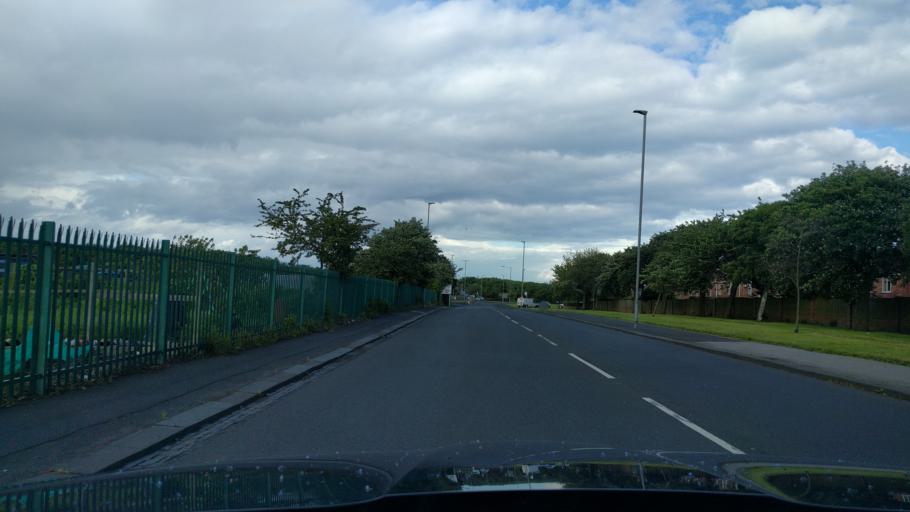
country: GB
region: England
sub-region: Northumberland
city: Lynemouth
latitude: 55.1865
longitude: -1.5541
